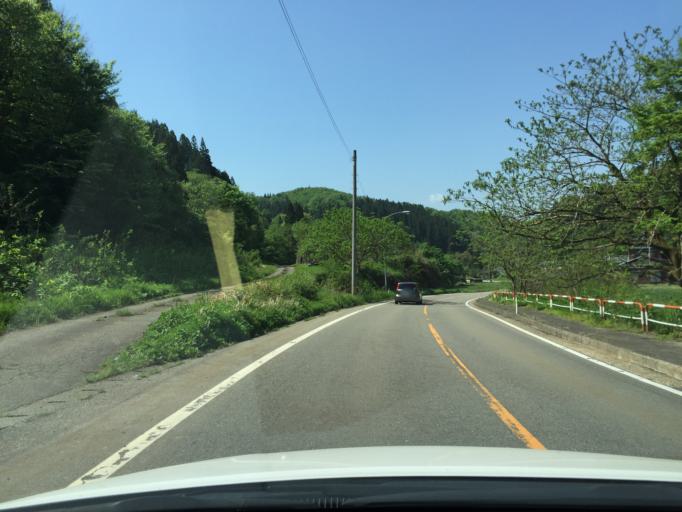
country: JP
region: Niigata
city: Muramatsu
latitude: 37.6387
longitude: 139.1116
